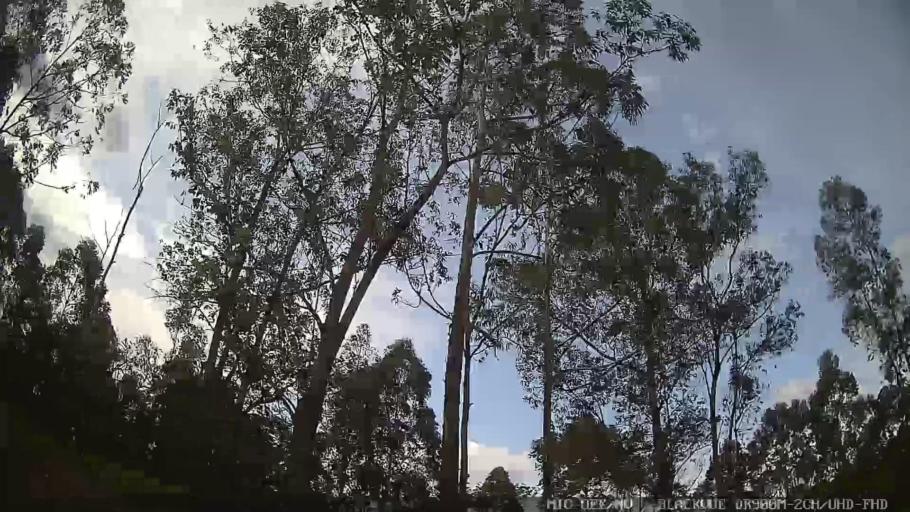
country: BR
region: Sao Paulo
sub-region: Amparo
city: Amparo
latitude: -22.7809
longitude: -46.7583
